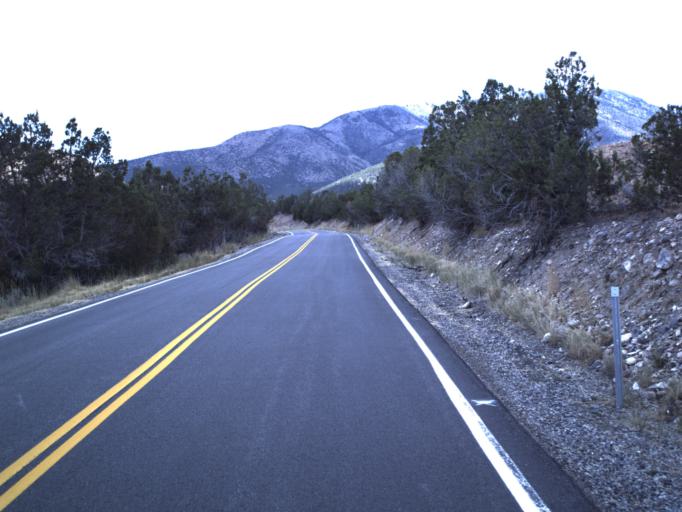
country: US
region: Utah
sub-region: Tooele County
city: Grantsville
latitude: 40.3362
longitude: -112.5299
